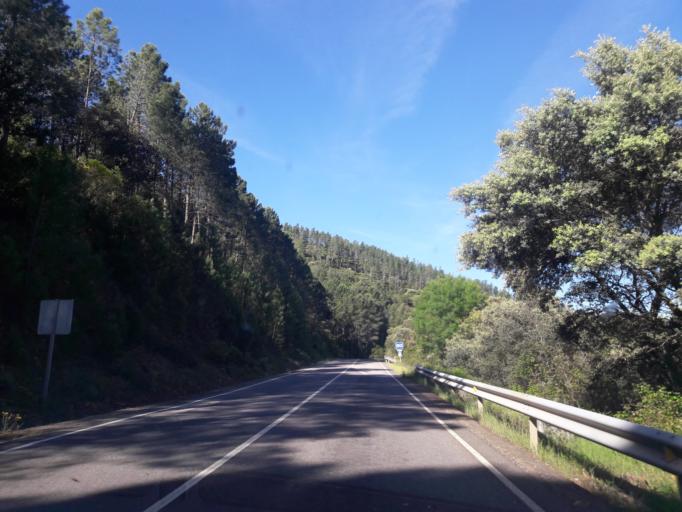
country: ES
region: Castille and Leon
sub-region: Provincia de Salamanca
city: Sotoserrano
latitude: 40.4058
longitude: -6.0534
